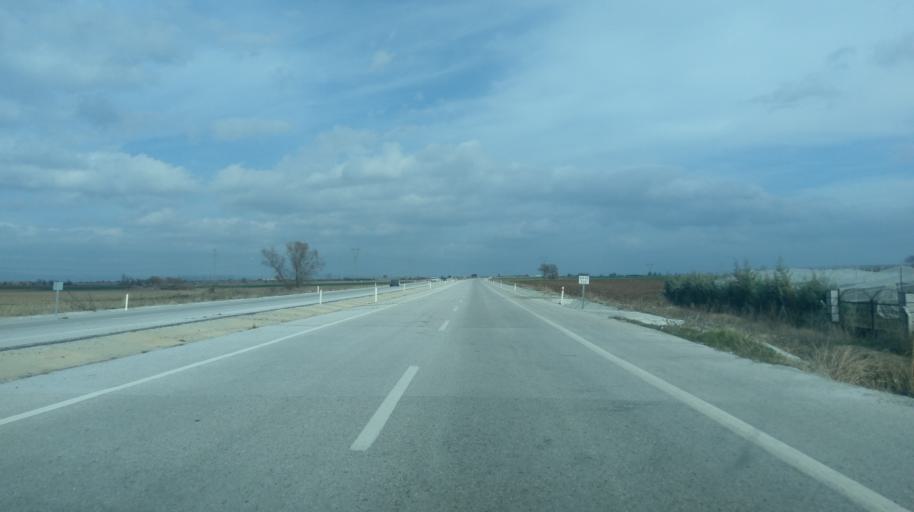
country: TR
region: Kirklareli
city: Inece
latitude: 41.6842
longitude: 27.1150
